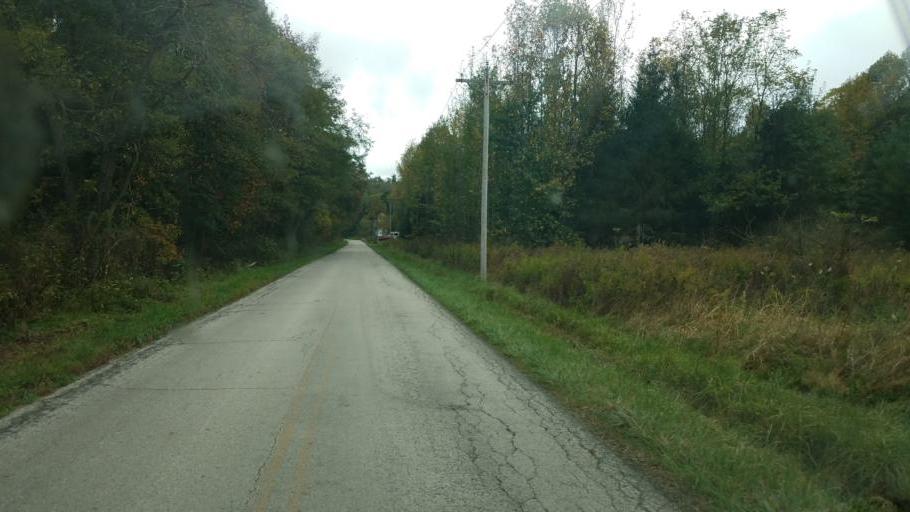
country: US
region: Ohio
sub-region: Ashland County
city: Loudonville
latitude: 40.5835
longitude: -82.1680
